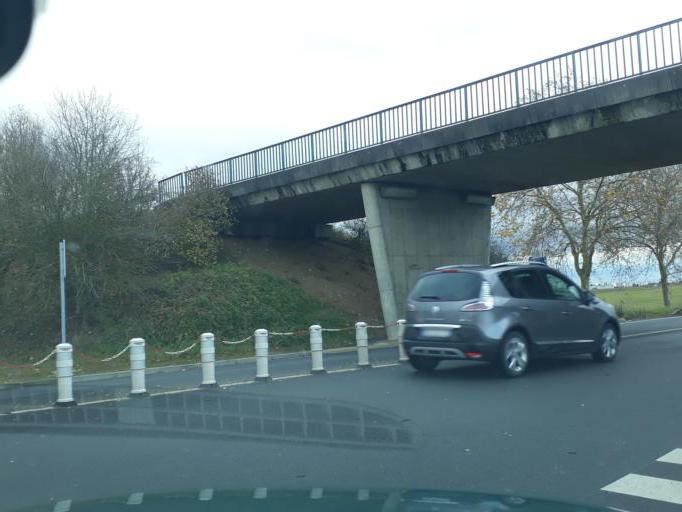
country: FR
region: Centre
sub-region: Departement du Loir-et-Cher
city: La Chaussee-Saint-Victor
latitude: 47.6209
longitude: 1.3464
